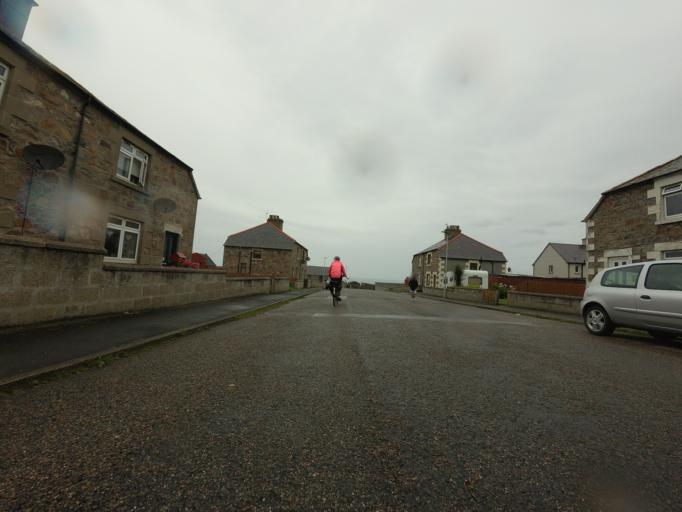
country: GB
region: Scotland
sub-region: Moray
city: Portknockie
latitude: 57.7041
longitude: -2.8558
